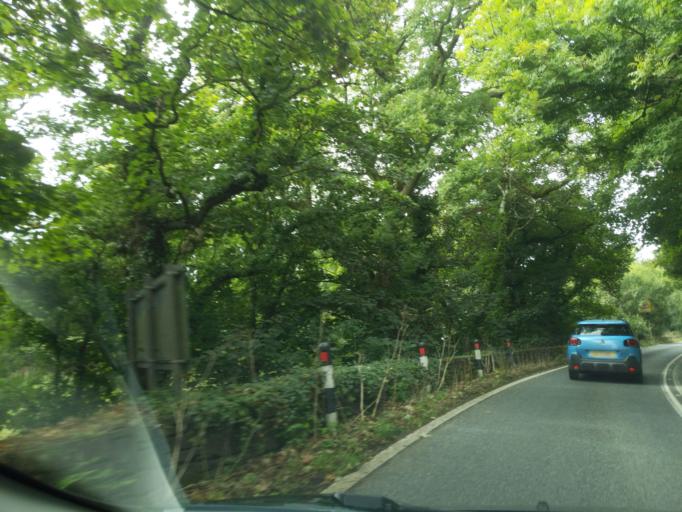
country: GB
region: England
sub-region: Cornwall
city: Porthleven
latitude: 50.1060
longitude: -5.3326
